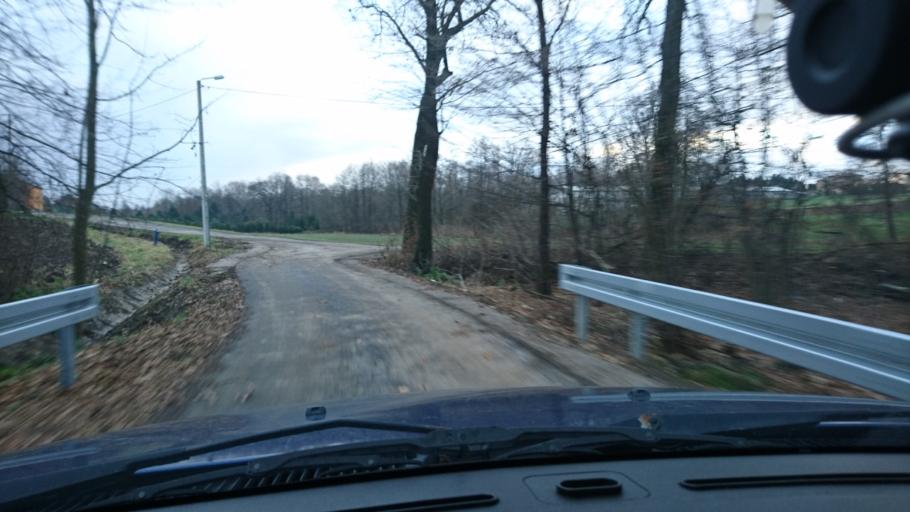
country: PL
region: Silesian Voivodeship
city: Janowice
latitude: 49.8946
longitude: 19.0809
